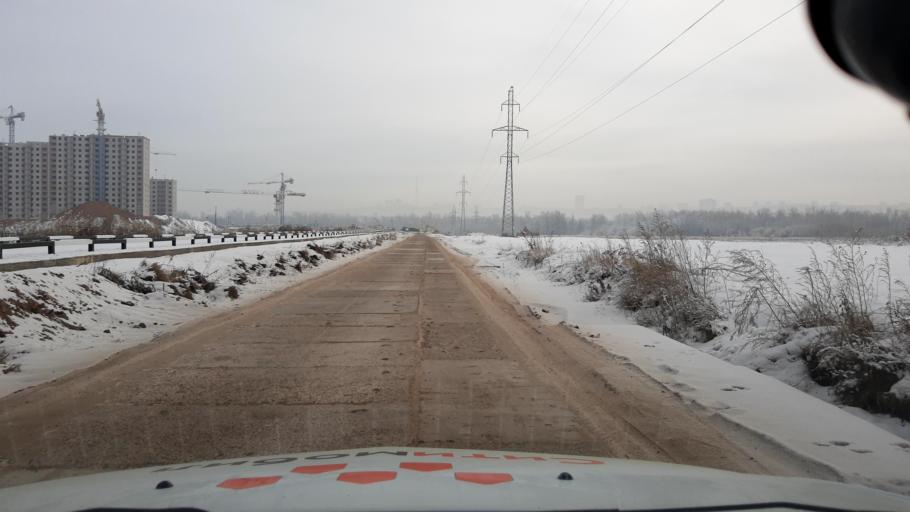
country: RU
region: Bashkortostan
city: Ufa
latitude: 54.7795
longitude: 55.9541
